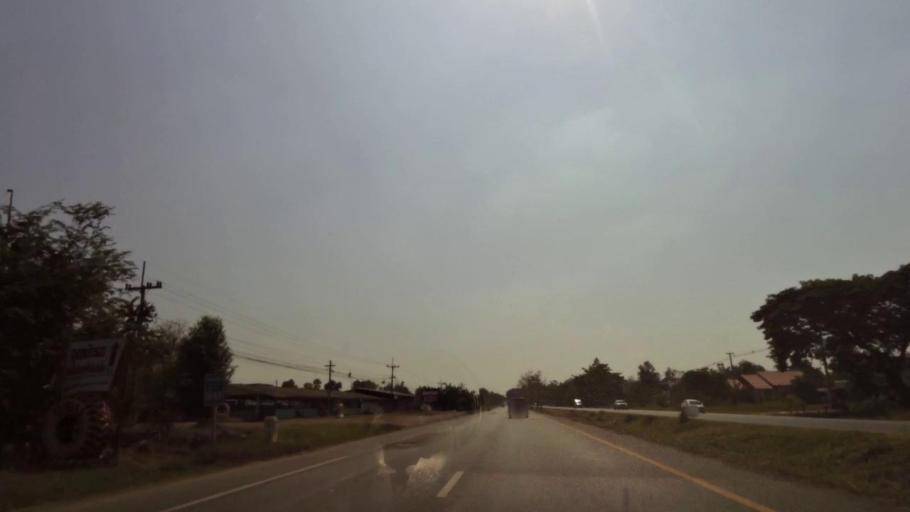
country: TH
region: Phichit
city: Bueng Na Rang
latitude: 16.3432
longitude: 100.1283
